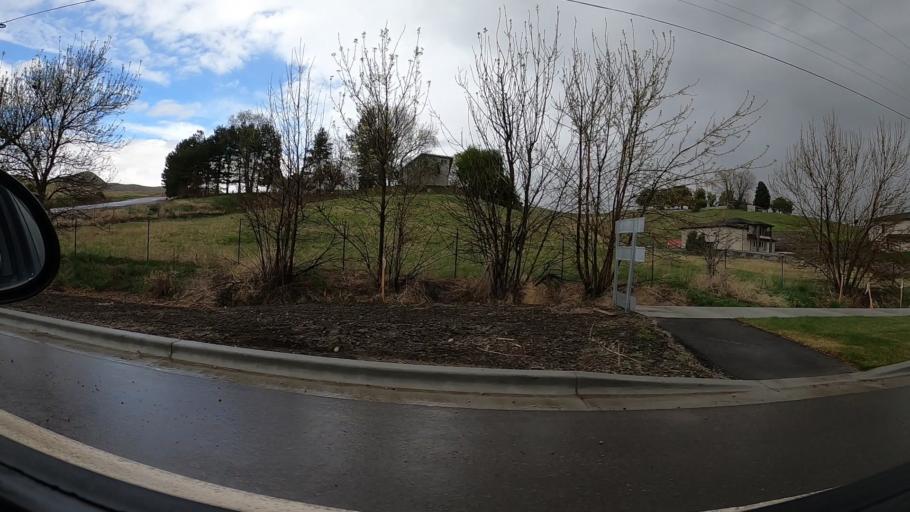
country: US
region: Idaho
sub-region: Ada County
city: Eagle
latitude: 43.7354
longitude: -116.2935
